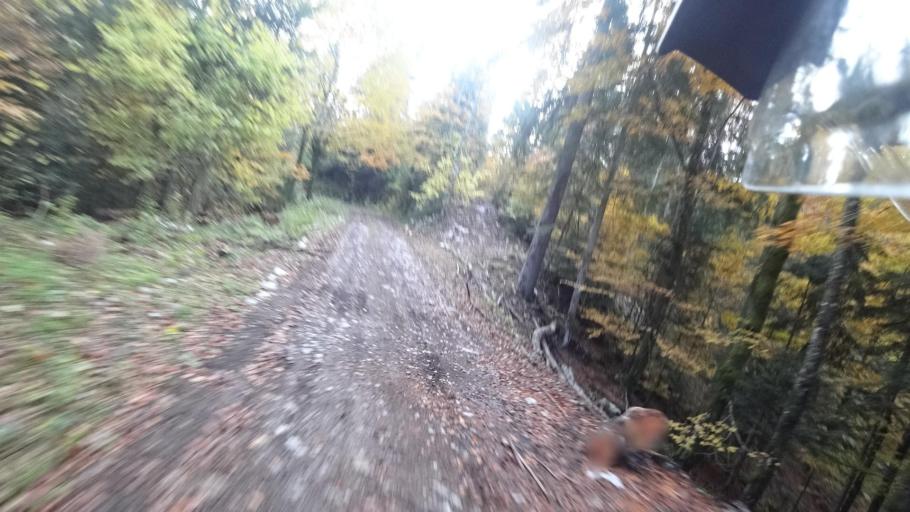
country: HR
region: Primorsko-Goranska
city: Vrbovsko
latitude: 45.2146
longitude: 15.0702
